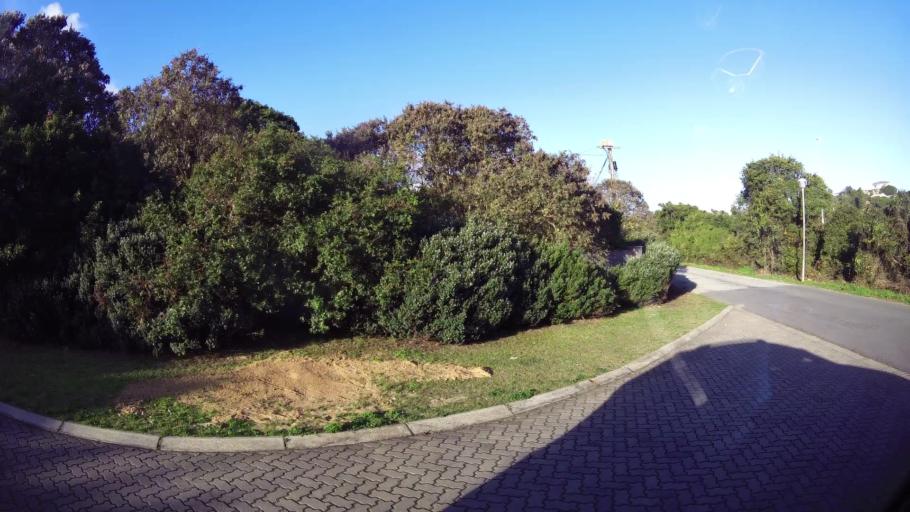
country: ZA
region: Western Cape
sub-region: Eden District Municipality
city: George
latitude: -33.9982
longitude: 22.6211
